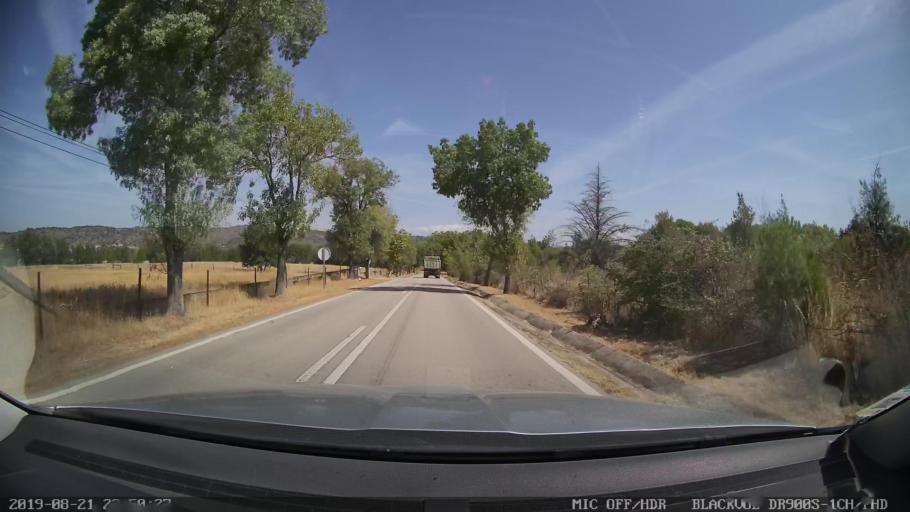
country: PT
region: Castelo Branco
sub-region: Idanha-A-Nova
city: Idanha-a-Nova
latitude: 39.8902
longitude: -7.2424
